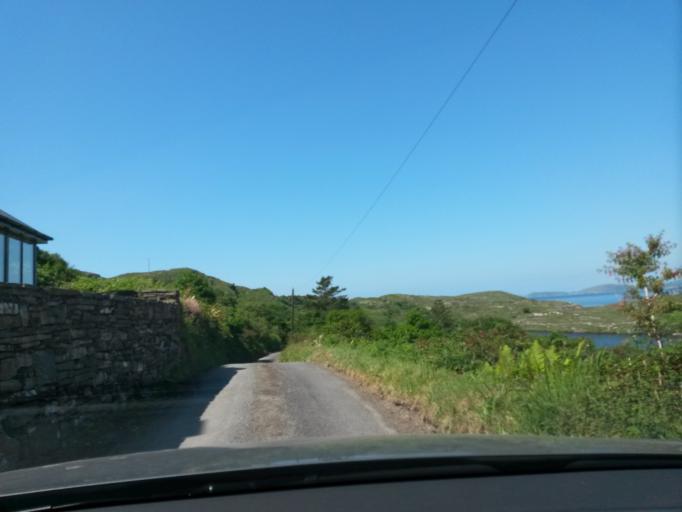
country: IE
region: Munster
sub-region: Ciarrai
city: Cahersiveen
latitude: 51.7343
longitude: -9.9550
